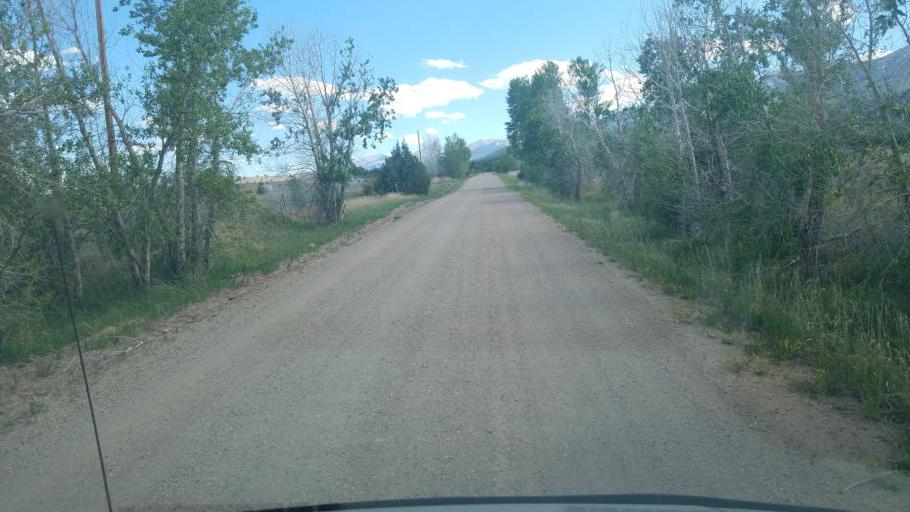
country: US
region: Colorado
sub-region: Custer County
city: Westcliffe
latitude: 38.2321
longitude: -105.5990
